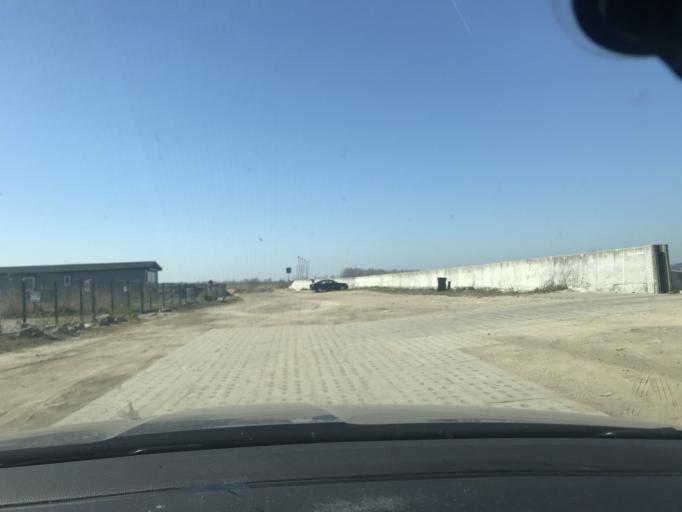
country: PL
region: Pomeranian Voivodeship
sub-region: Powiat pucki
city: Mosty
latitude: 54.6310
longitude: 18.4928
